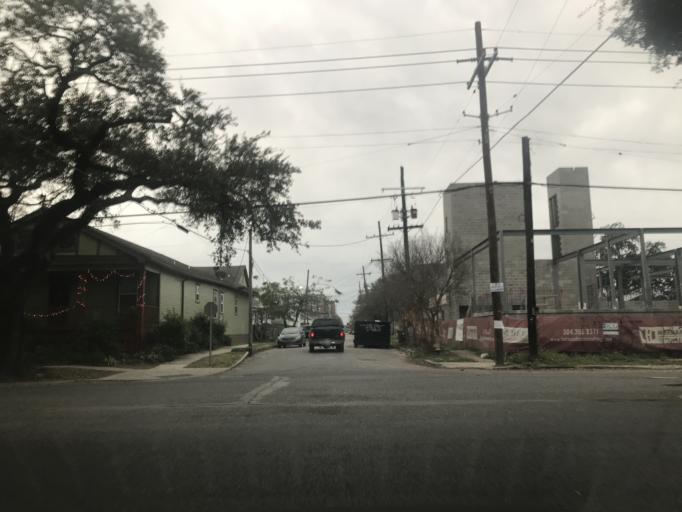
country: US
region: Louisiana
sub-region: Orleans Parish
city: New Orleans
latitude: 29.9657
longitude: -90.0936
